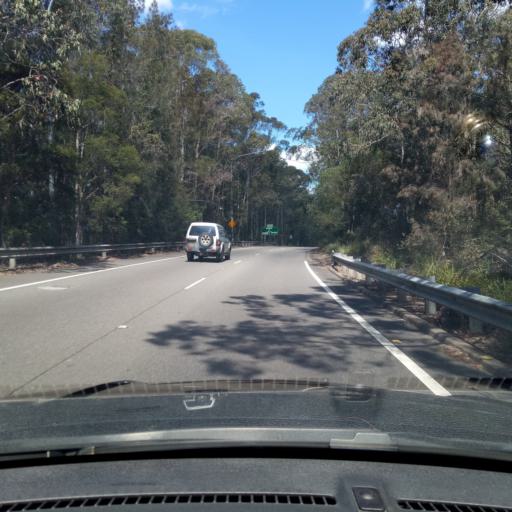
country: AU
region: New South Wales
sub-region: Wyong Shire
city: Chittaway Bay
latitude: -33.3340
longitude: 151.4318
